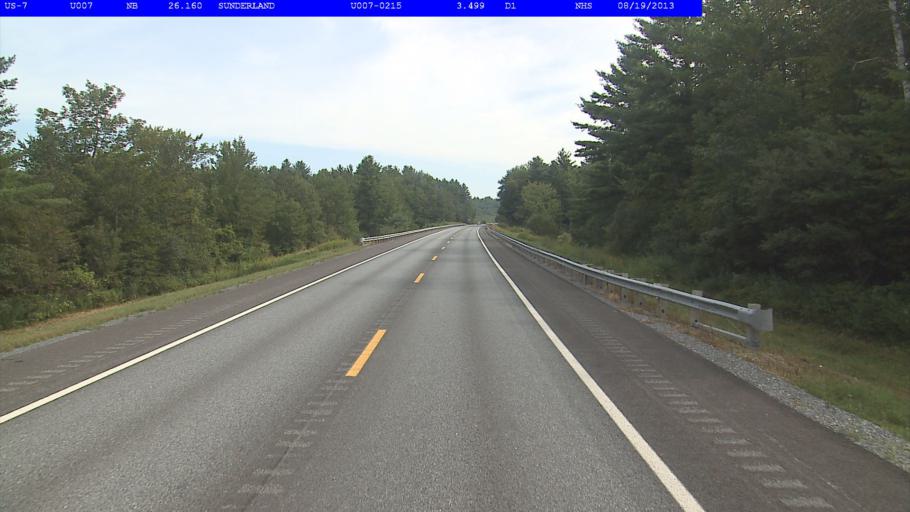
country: US
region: Vermont
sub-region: Bennington County
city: Arlington
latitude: 43.0741
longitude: -73.1198
